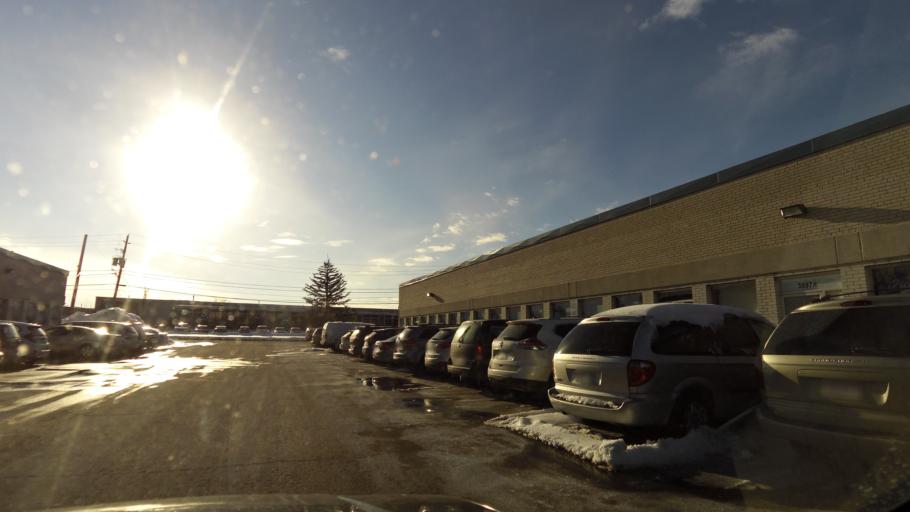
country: CA
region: Ontario
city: Etobicoke
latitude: 43.6241
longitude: -79.5714
